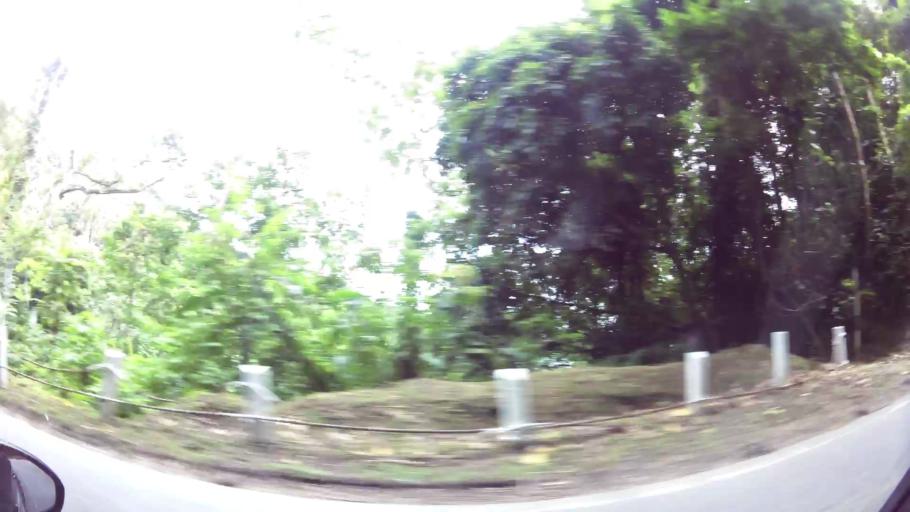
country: TT
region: Diego Martin
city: Petit Valley
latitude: 10.7435
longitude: -61.4943
